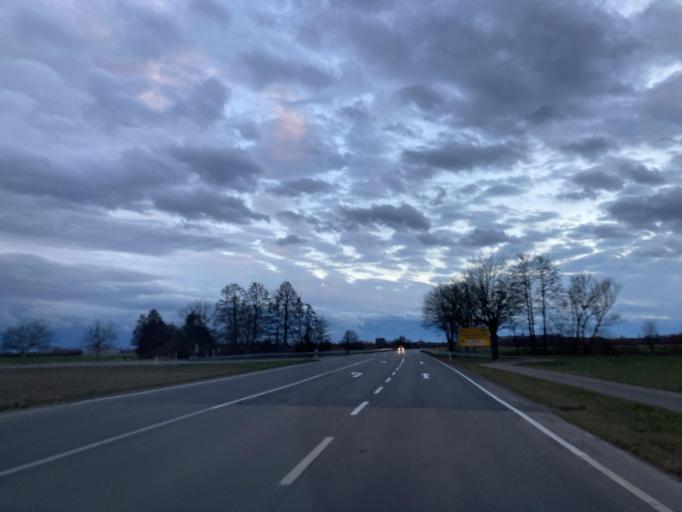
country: DE
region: Baden-Wuerttemberg
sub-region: Freiburg Region
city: Breisach am Rhein
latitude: 48.0539
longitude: 7.5921
